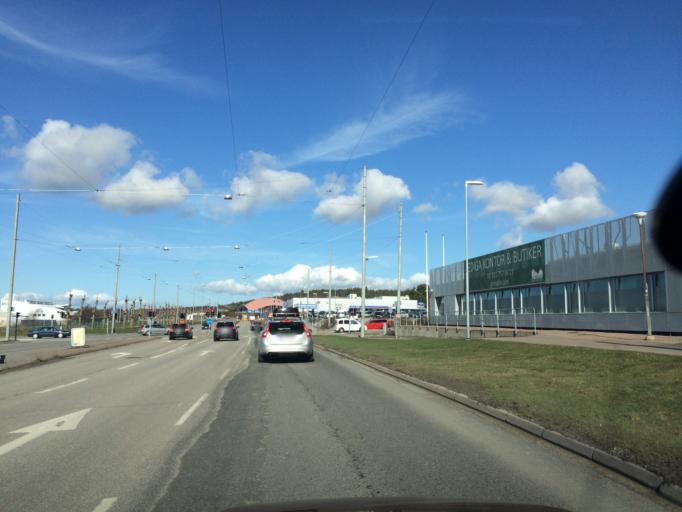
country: SE
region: Vaestra Goetaland
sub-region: Goteborg
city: Majorna
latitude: 57.7193
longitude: 11.8481
